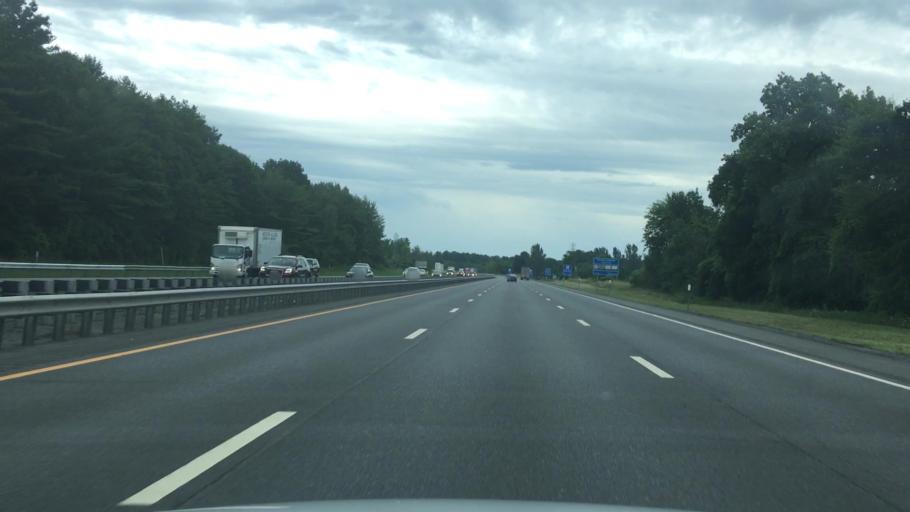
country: US
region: New York
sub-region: Schenectady County
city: Rotterdam
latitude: 42.7797
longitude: -74.0029
